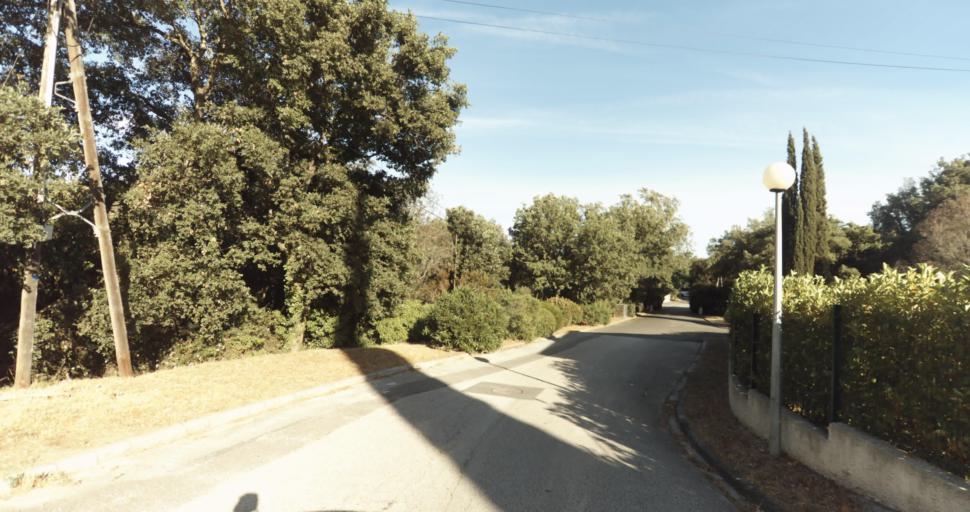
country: FR
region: Provence-Alpes-Cote d'Azur
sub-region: Departement du Var
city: La Croix-Valmer
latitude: 43.2240
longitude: 6.5686
